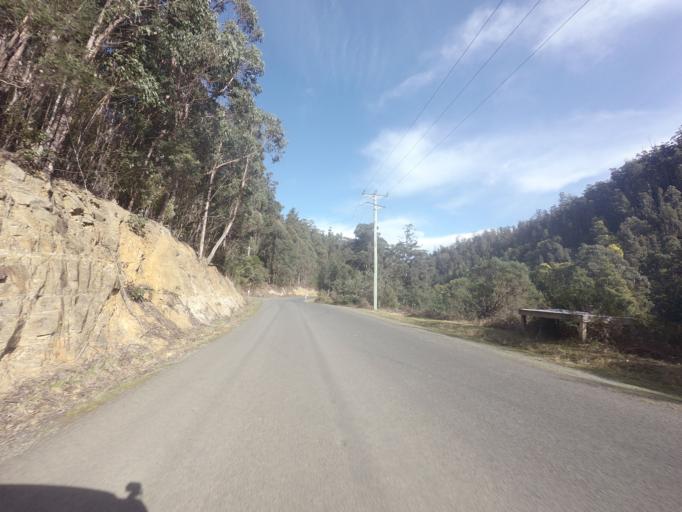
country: AU
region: Tasmania
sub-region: Huon Valley
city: Huonville
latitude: -43.0382
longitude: 147.1383
